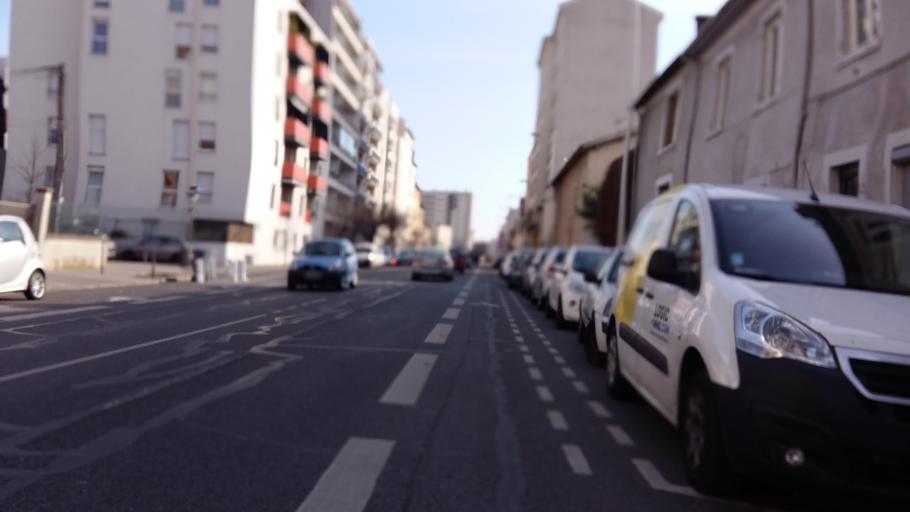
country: FR
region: Rhone-Alpes
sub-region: Departement du Rhone
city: Lyon
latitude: 45.7332
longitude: 4.8584
